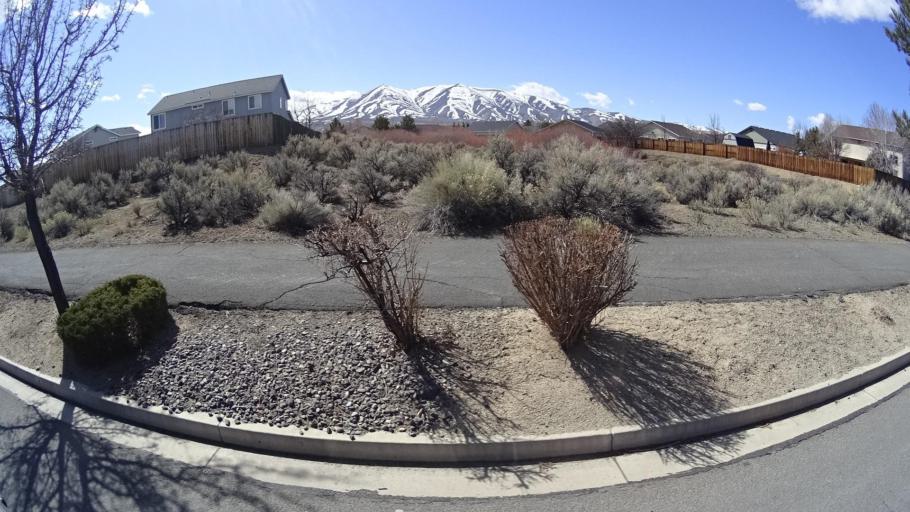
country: US
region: Nevada
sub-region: Washoe County
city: Lemmon Valley
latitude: 39.6343
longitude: -119.8659
